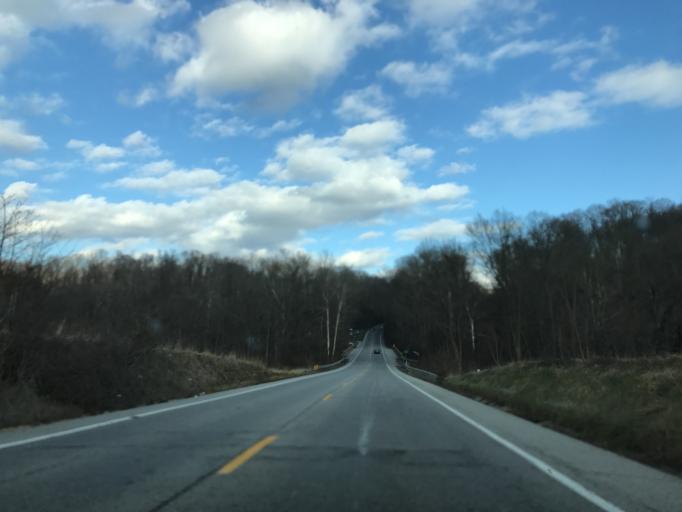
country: US
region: Maryland
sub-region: Cecil County
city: Rising Sun
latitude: 39.6926
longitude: -76.1267
